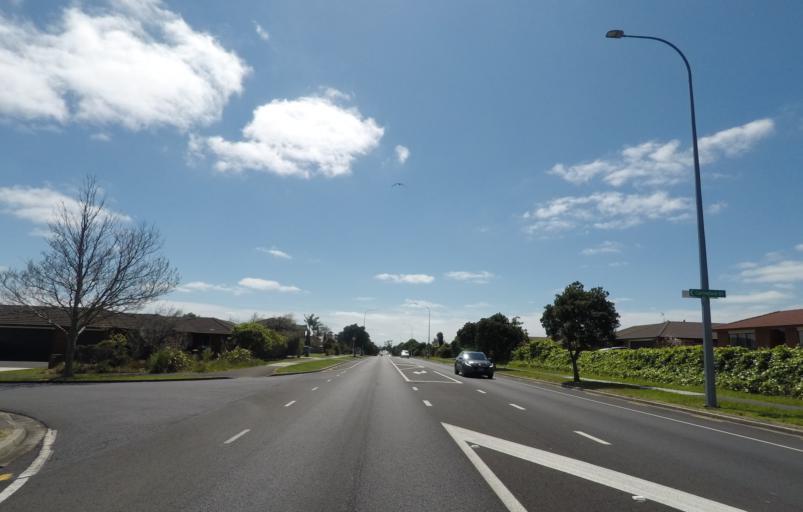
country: NZ
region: Auckland
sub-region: Auckland
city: Pakuranga
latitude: -36.9411
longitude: 174.9131
